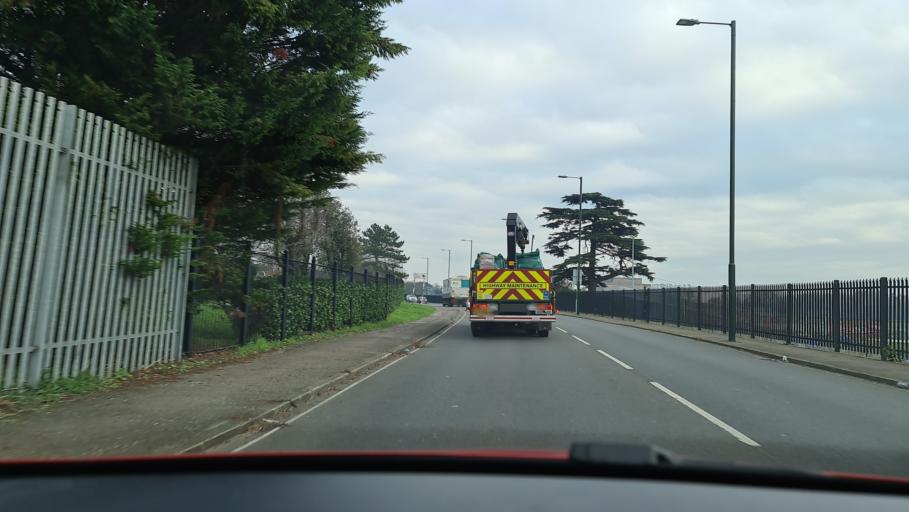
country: GB
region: England
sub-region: Greater London
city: Hampton
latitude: 51.4136
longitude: -0.3797
